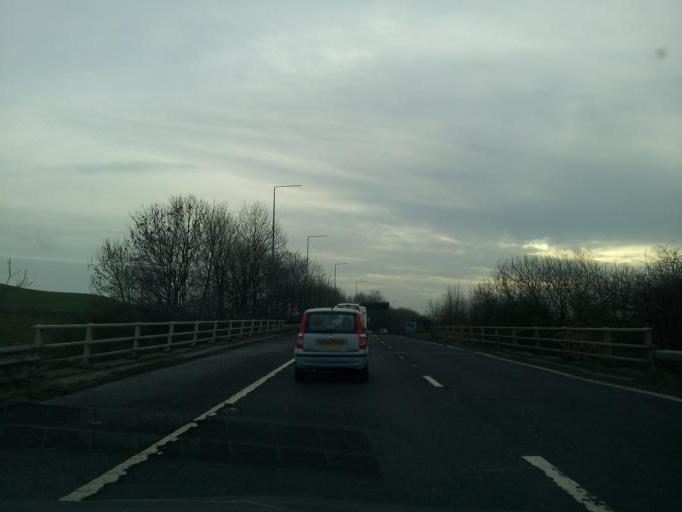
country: GB
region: England
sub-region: Borough of Rochdale
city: Rochdale
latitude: 53.5857
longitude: -2.1567
